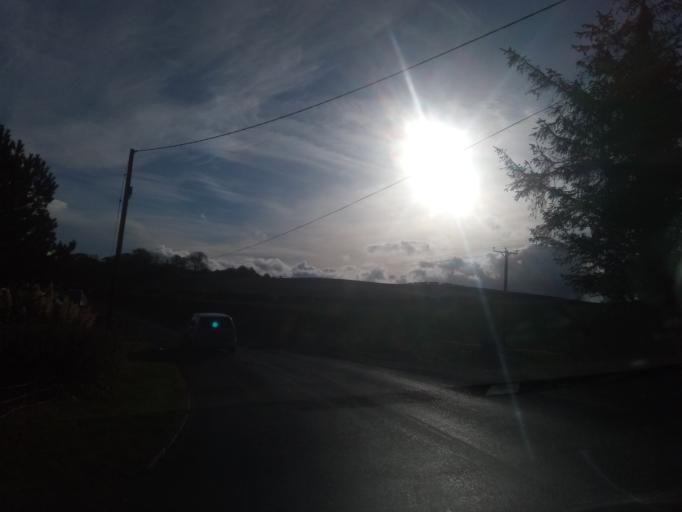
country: GB
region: Scotland
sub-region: The Scottish Borders
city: Eyemouth
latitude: 55.8574
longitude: -2.0992
